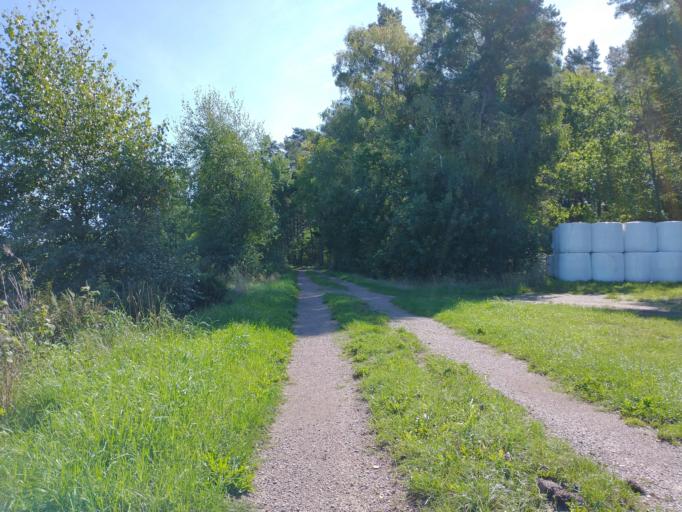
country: SE
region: Kalmar
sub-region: Kalmar Kommun
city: Lindsdal
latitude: 56.7863
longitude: 16.2834
